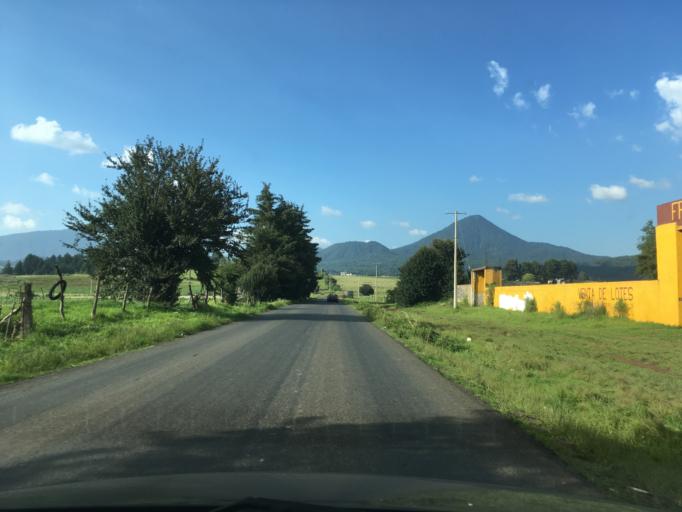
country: MX
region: Michoacan
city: Nahuatzen
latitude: 19.6426
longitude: -101.9241
